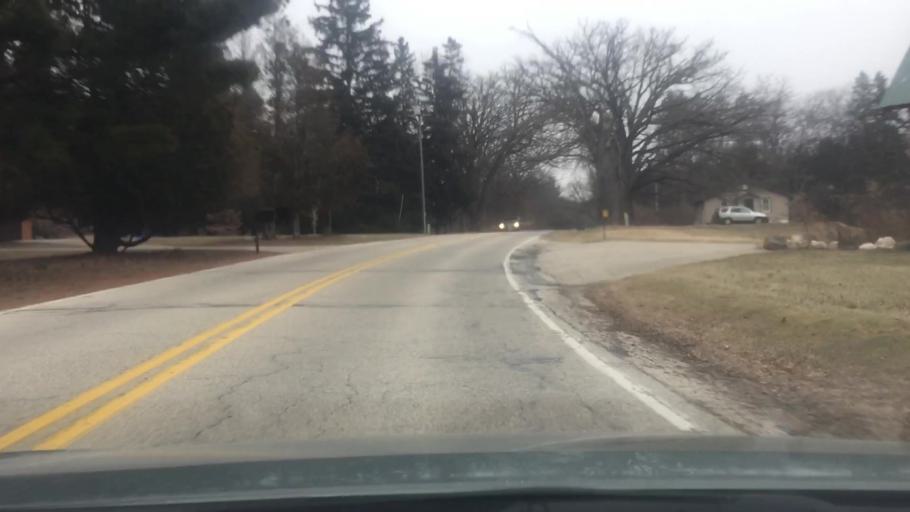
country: US
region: Wisconsin
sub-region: Waukesha County
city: Eagle
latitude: 42.9370
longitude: -88.4638
